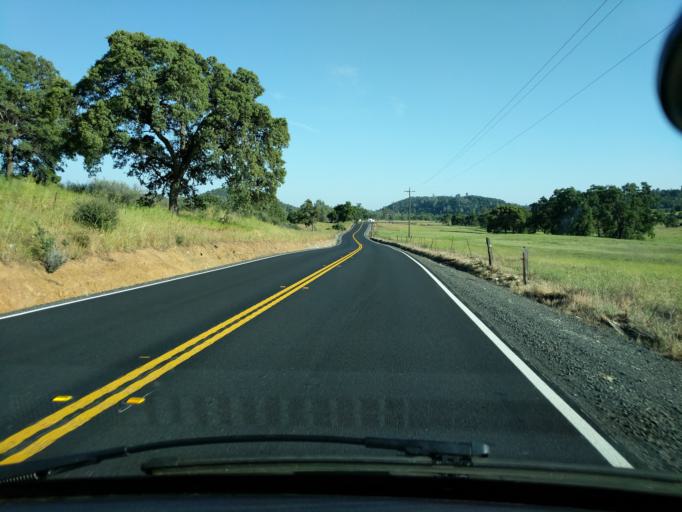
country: US
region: California
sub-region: Calaveras County
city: Copperopolis
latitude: 38.0242
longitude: -120.6449
